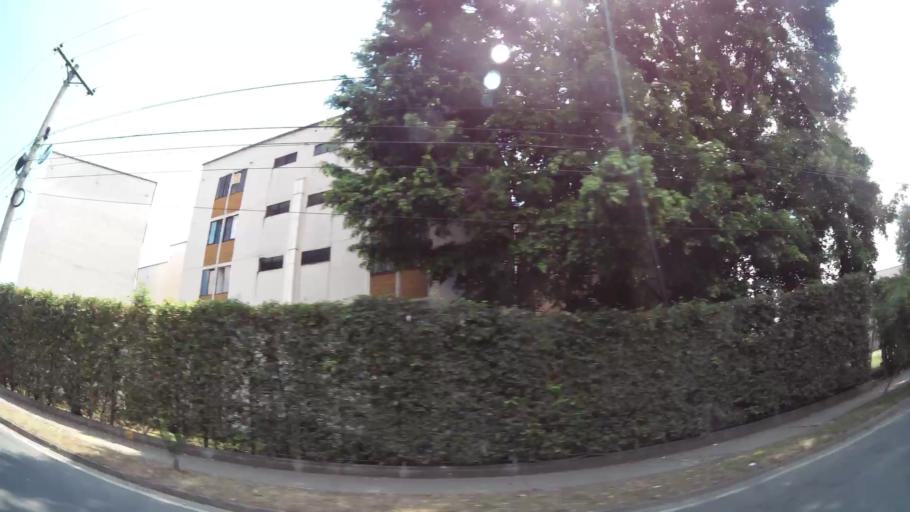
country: CO
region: Valle del Cauca
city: Cali
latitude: 3.4526
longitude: -76.4918
